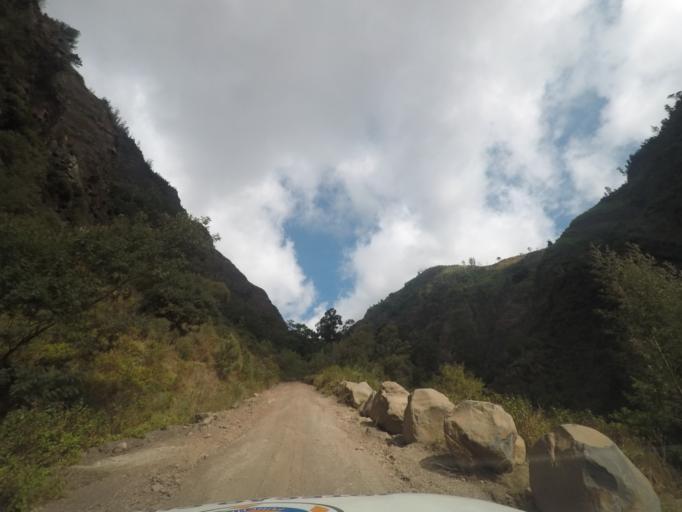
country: PT
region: Madeira
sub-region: Funchal
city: Nossa Senhora do Monte
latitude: 32.6897
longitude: -16.9174
